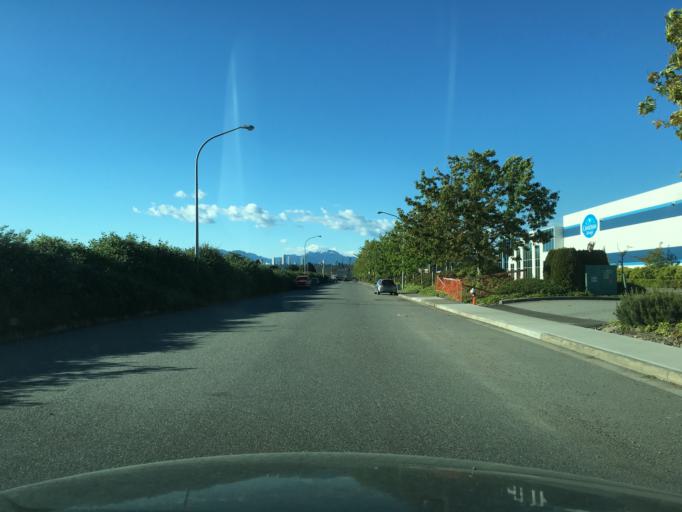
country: CA
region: British Columbia
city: Delta
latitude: 49.1662
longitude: -122.9940
